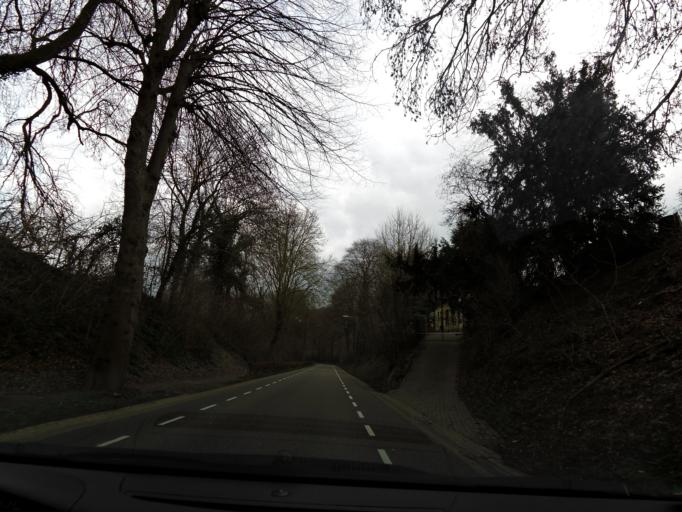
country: NL
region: Limburg
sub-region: Valkenburg aan de Geul
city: Sibbe
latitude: 50.8535
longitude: 5.8226
